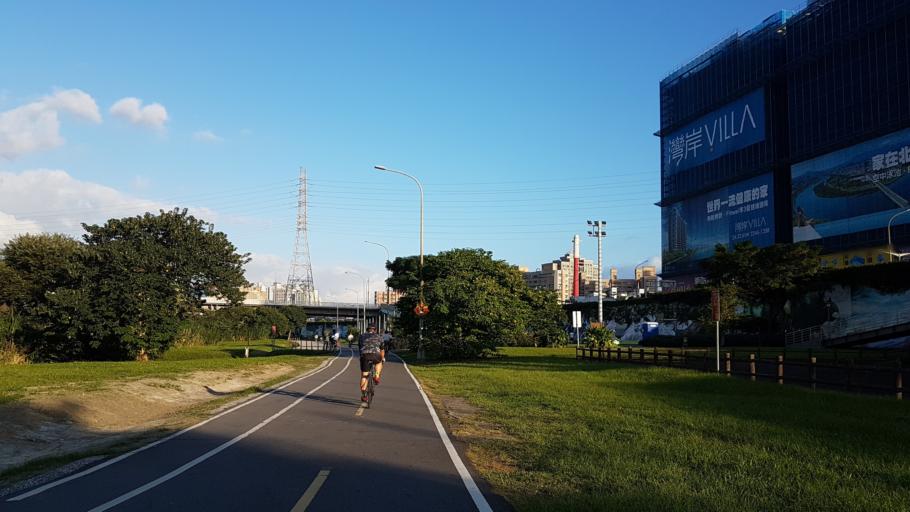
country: TW
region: Taipei
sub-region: Taipei
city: Banqiao
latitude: 25.0085
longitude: 121.4931
